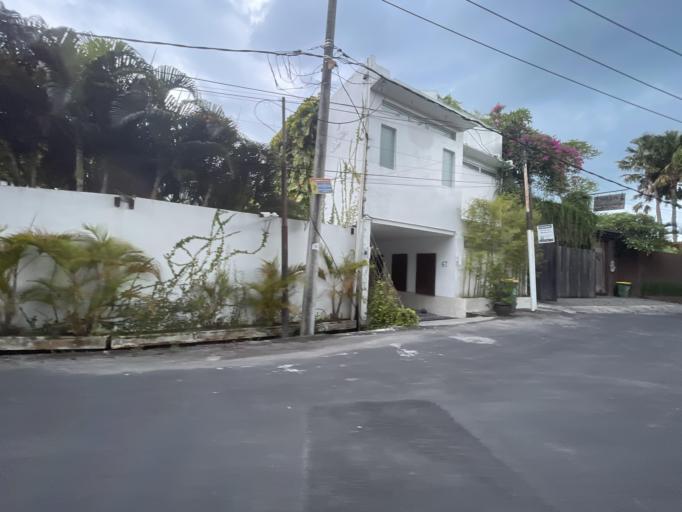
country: ID
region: Bali
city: Banjar Gunungpande
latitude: -8.6675
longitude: 115.1438
